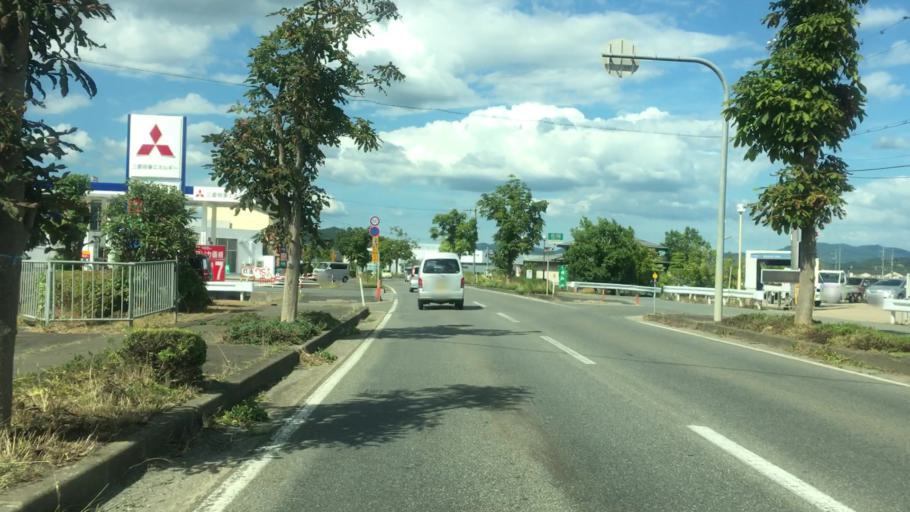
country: JP
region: Hyogo
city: Toyooka
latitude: 35.4799
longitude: 134.7832
